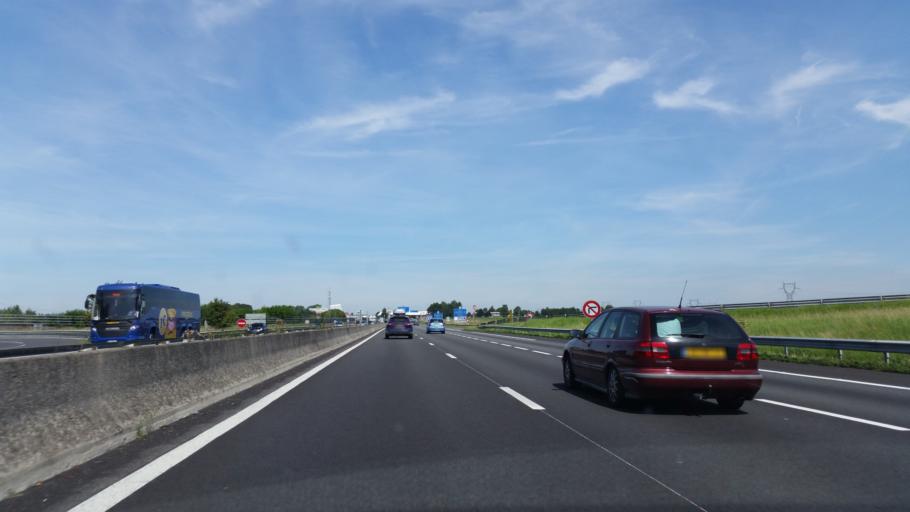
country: FR
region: Picardie
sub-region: Departement de la Somme
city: Chaulnes
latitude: 49.8788
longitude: 2.8370
